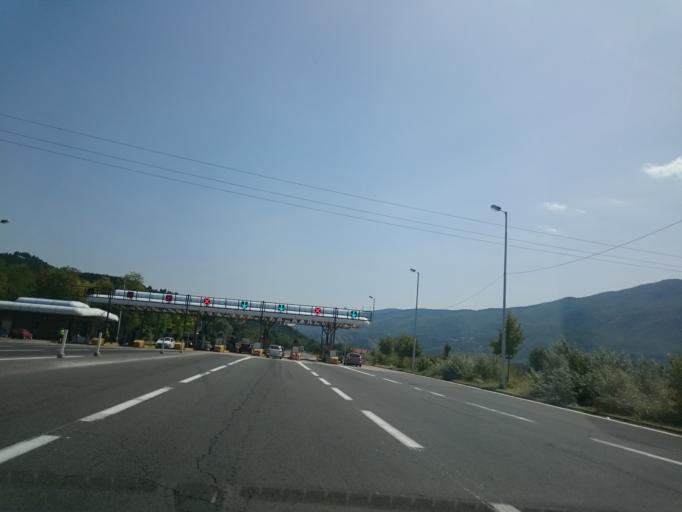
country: MK
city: Ljubin
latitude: 41.9885
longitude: 21.2917
